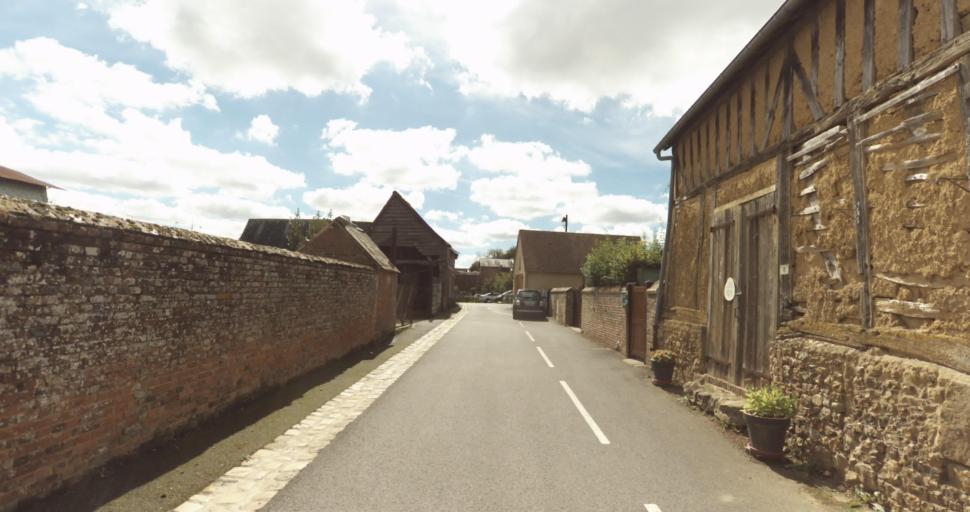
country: FR
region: Lower Normandy
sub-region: Departement de l'Orne
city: Gace
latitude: 48.8933
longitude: 0.3368
